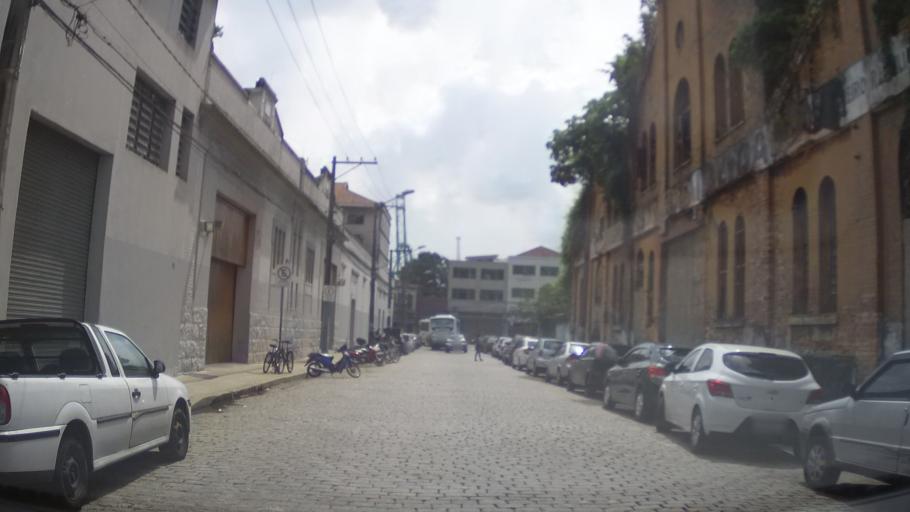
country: BR
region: Sao Paulo
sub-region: Santos
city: Santos
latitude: -23.9344
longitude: -46.3336
